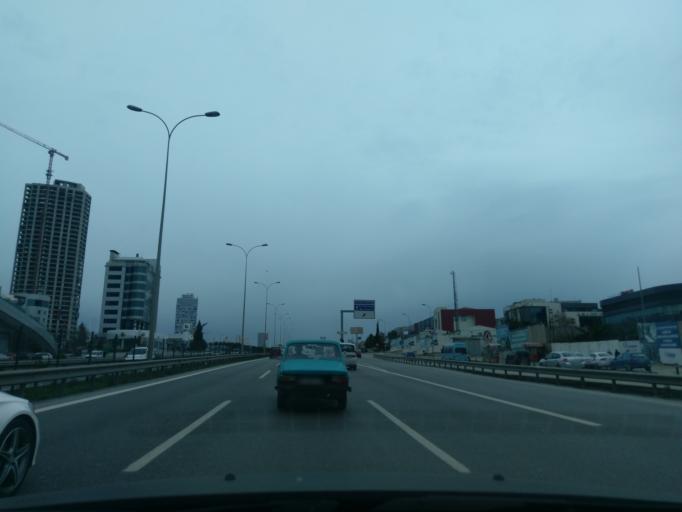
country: TR
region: Istanbul
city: Maltepe
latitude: 40.9178
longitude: 29.1745
